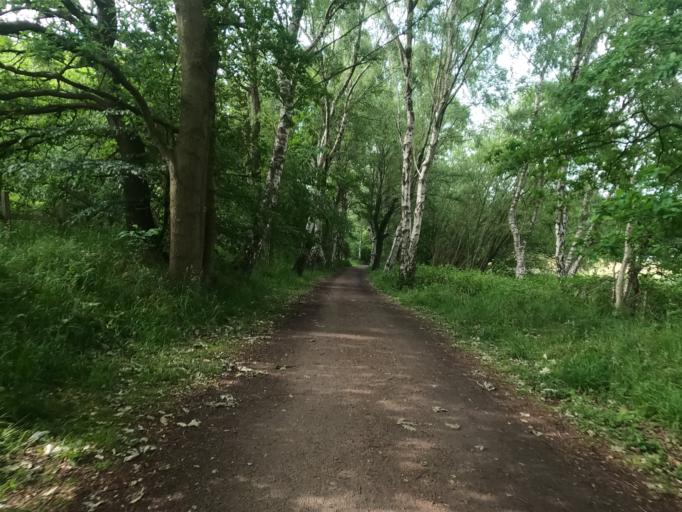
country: GB
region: England
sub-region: Cheshire West and Chester
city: Cuddington
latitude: 53.2255
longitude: -2.6193
